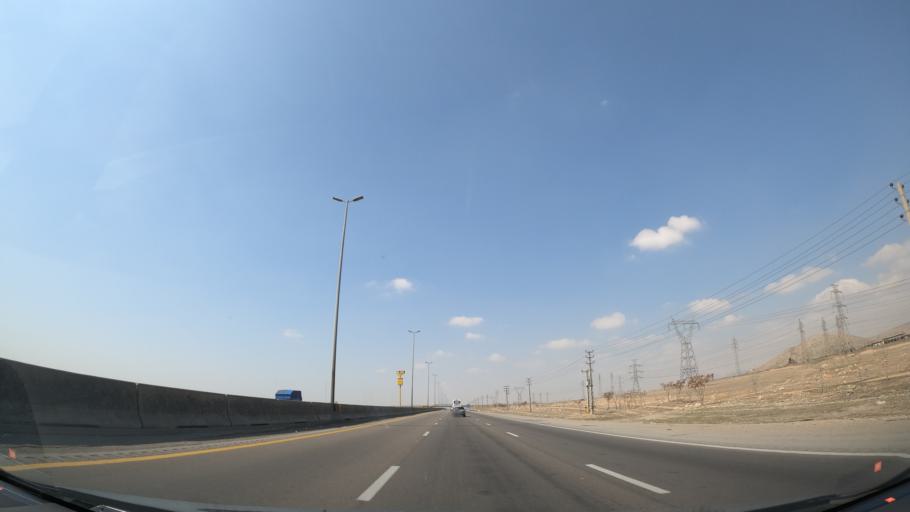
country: IR
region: Qazvin
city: Abyek
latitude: 36.0615
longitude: 50.4959
